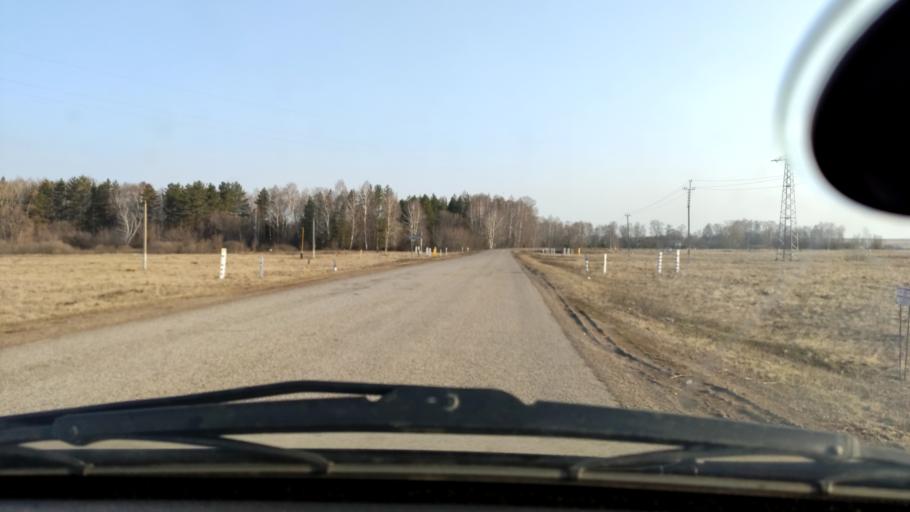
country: RU
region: Bashkortostan
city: Asanovo
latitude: 54.7708
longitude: 55.4880
